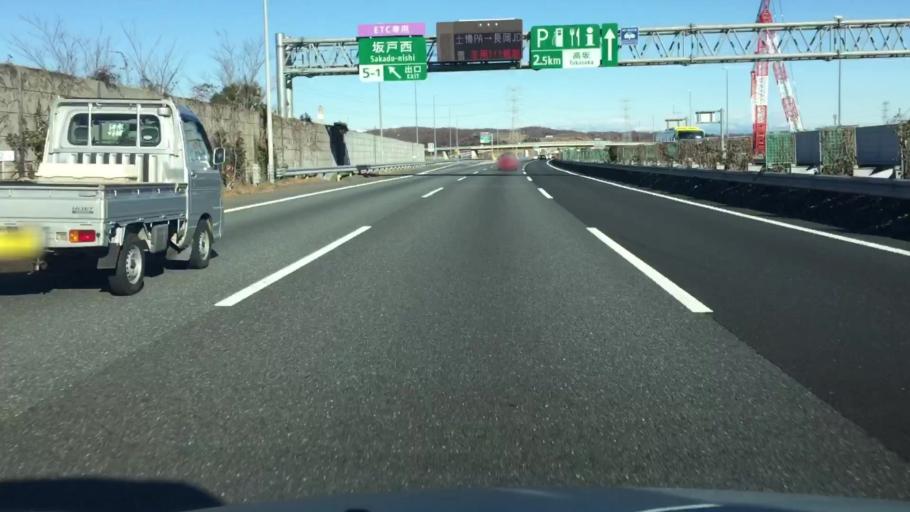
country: JP
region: Saitama
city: Sakado
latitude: 35.9627
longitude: 139.3806
